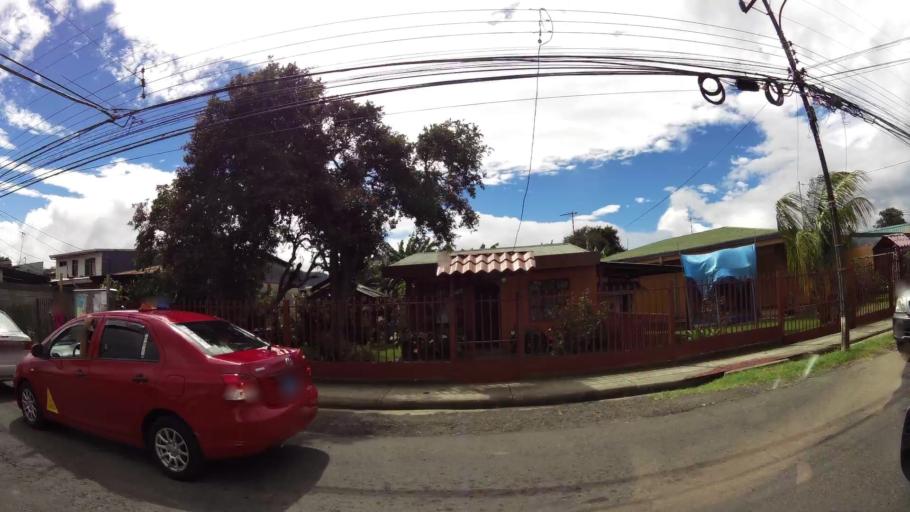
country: CR
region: Cartago
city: Concepcion
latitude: 9.9216
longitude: -83.9950
